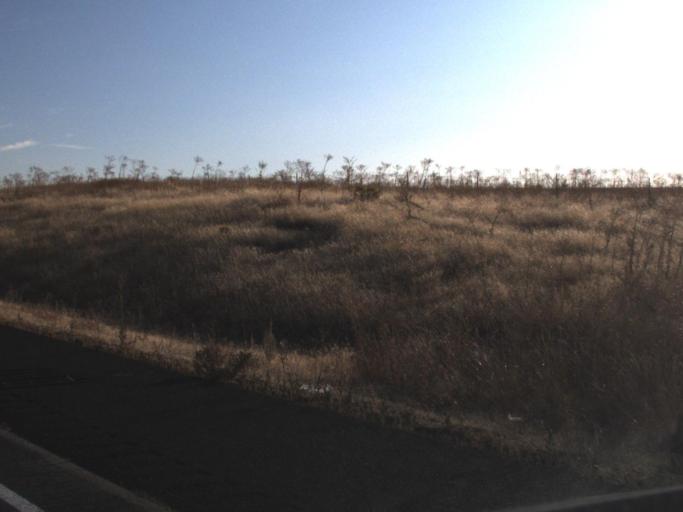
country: US
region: Washington
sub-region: Franklin County
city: Connell
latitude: 46.6161
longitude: -118.9042
